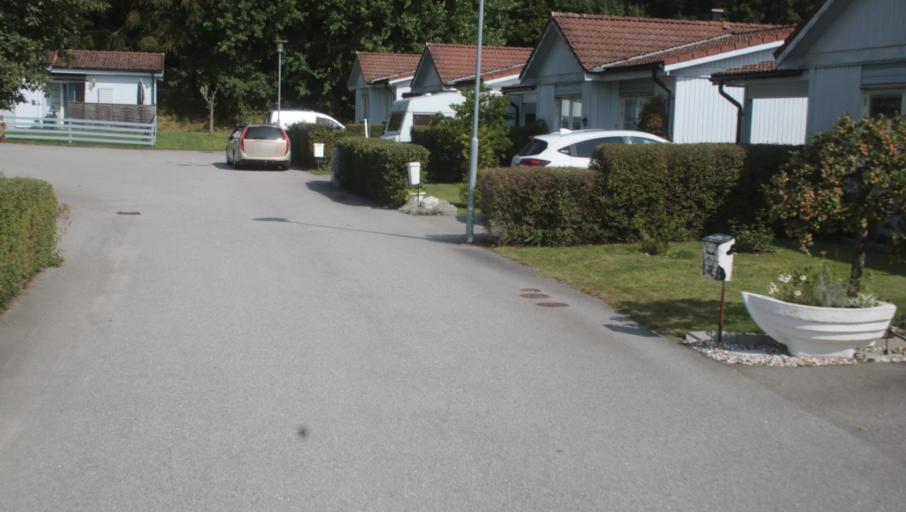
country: SE
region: Blekinge
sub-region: Karlshamns Kommun
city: Karlshamn
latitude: 56.1995
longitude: 14.8482
